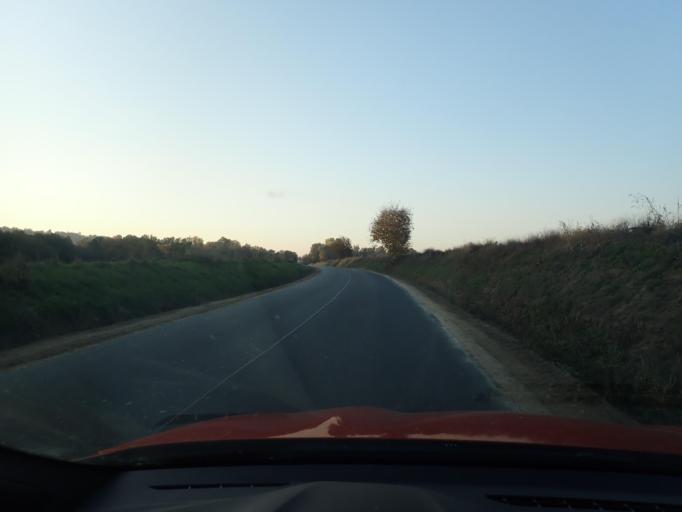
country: HU
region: Baranya
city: Kozarmisleny
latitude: 46.0226
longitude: 18.4039
